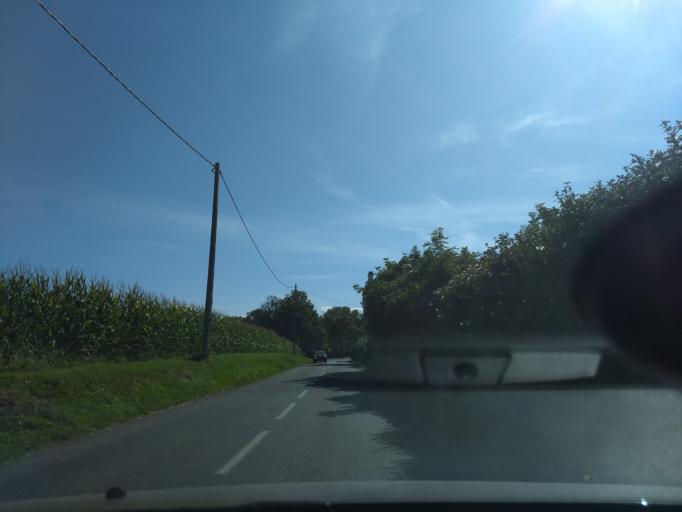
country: FR
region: Aquitaine
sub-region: Departement des Pyrenees-Atlantiques
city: Soumoulou
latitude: 43.2793
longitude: -0.1796
